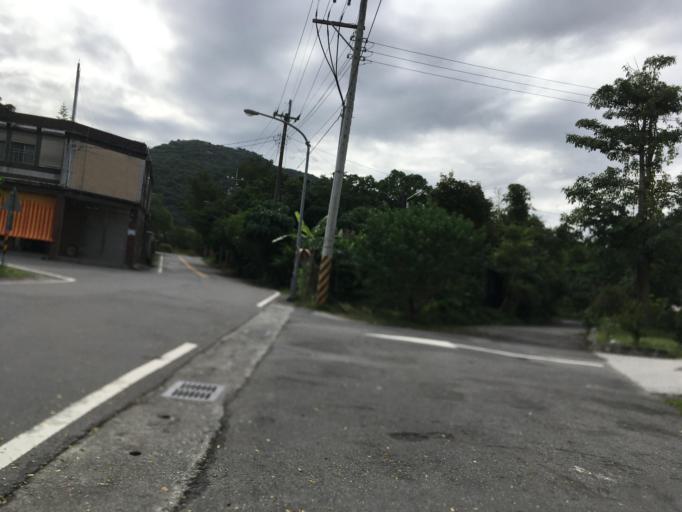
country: TW
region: Taiwan
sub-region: Yilan
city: Yilan
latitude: 24.6136
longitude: 121.8535
